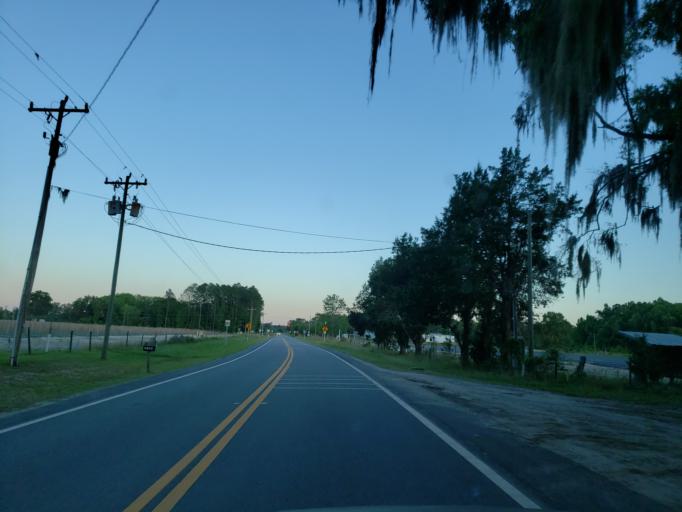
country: US
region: Georgia
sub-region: Echols County
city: Statenville
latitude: 30.5706
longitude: -83.1616
